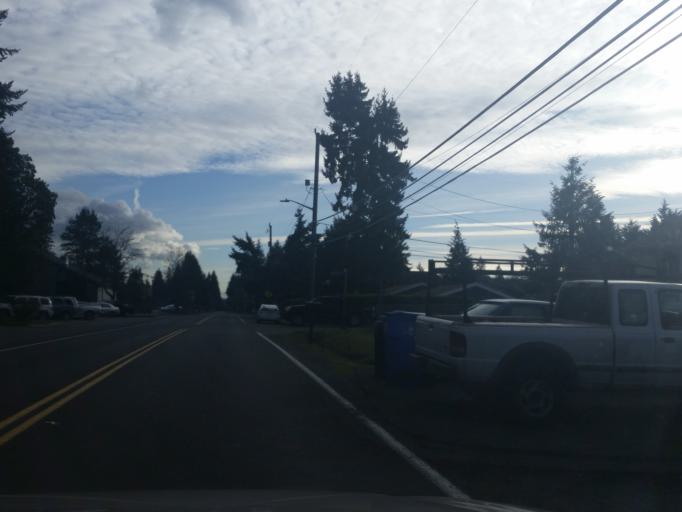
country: US
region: Washington
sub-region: King County
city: Shoreline
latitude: 47.7685
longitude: -122.3298
